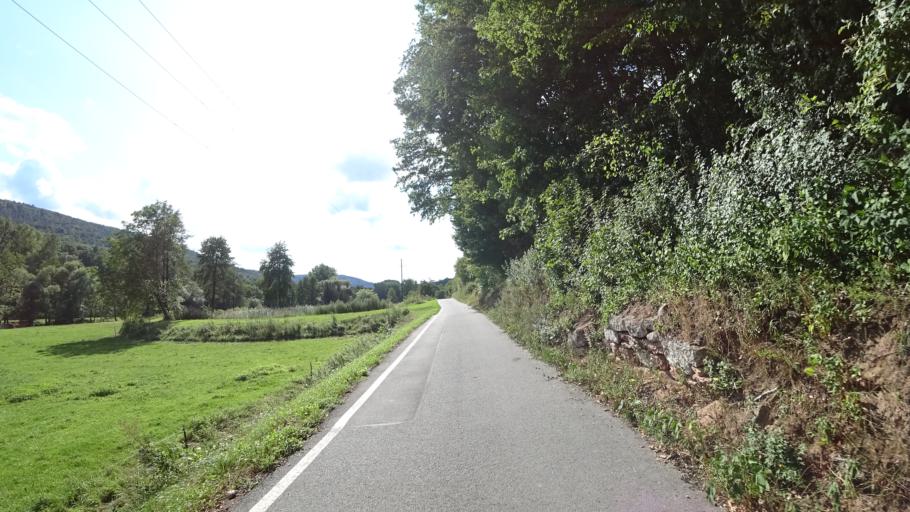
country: DE
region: Bavaria
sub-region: Regierungsbezirk Unterfranken
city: Eichenbuhl
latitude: 49.7089
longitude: 9.3036
